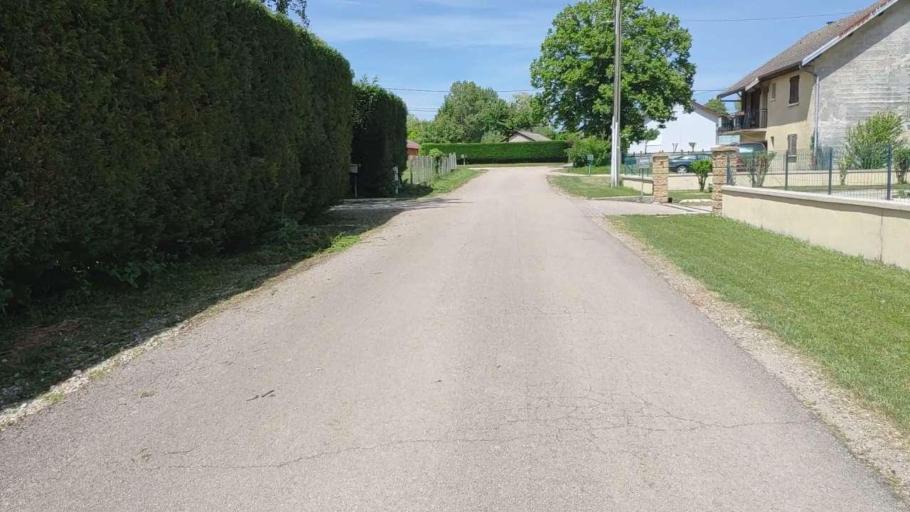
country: FR
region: Franche-Comte
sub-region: Departement du Jura
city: Bletterans
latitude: 46.7612
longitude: 5.4451
